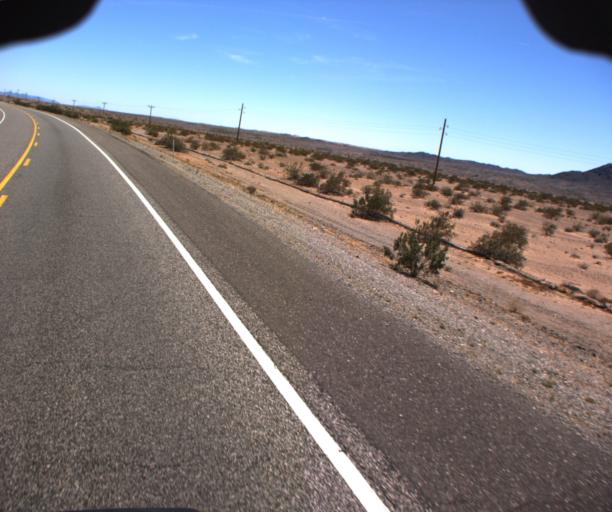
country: US
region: Arizona
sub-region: La Paz County
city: Parker
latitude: 34.0313
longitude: -114.2580
